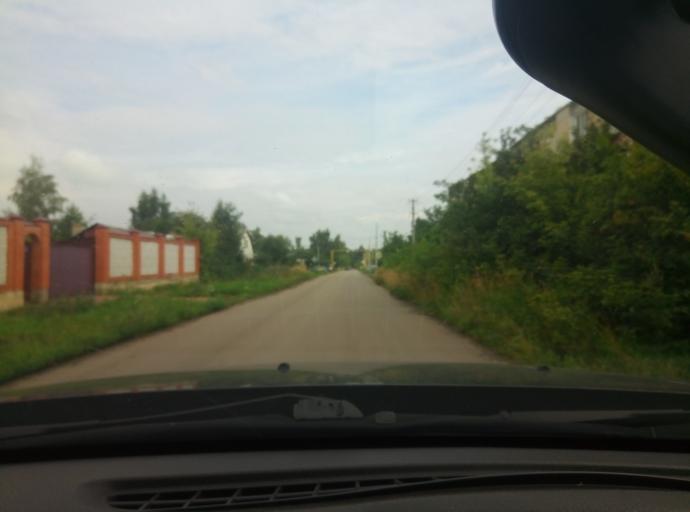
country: RU
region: Tula
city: Kimovsk
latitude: 53.9749
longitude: 38.5225
